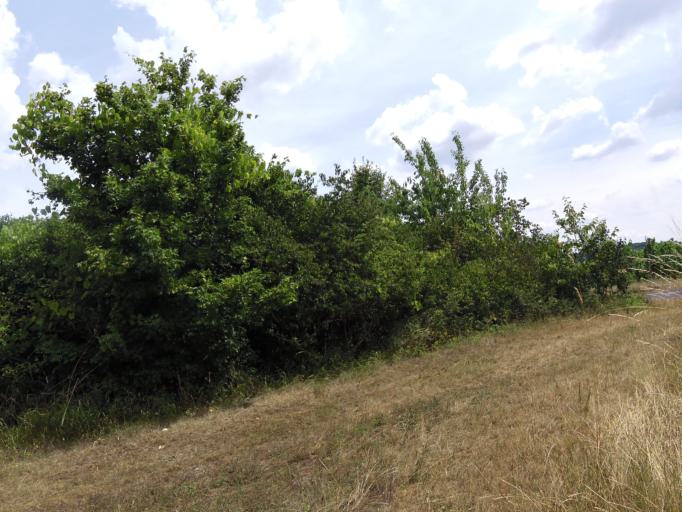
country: DE
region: Bavaria
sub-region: Regierungsbezirk Unterfranken
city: Randersacker
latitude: 49.7653
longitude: 9.9836
